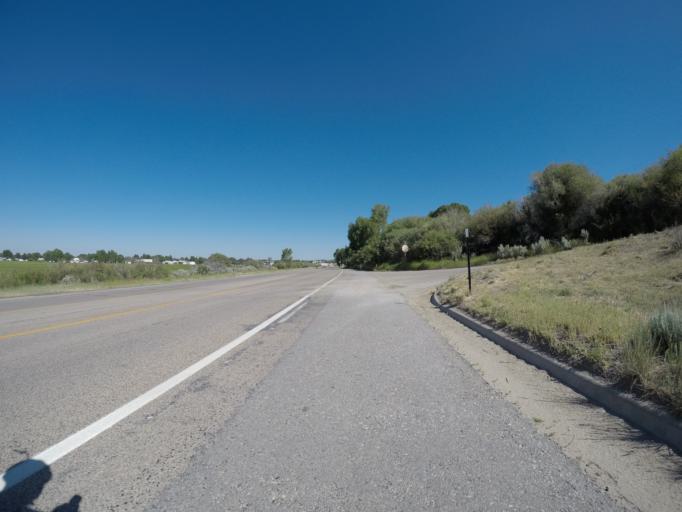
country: US
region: Wyoming
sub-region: Sublette County
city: Pinedale
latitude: 42.8611
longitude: -109.8515
